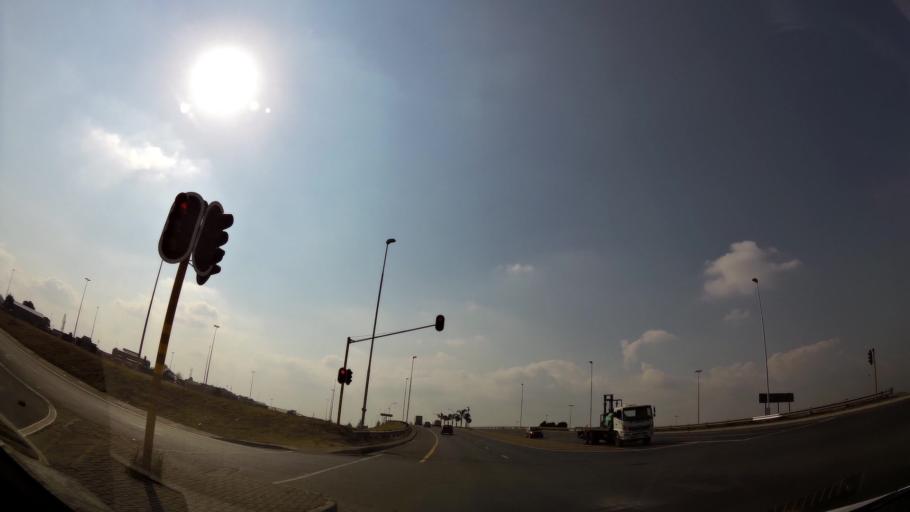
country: ZA
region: Gauteng
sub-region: Ekurhuleni Metropolitan Municipality
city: Germiston
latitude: -26.1767
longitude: 28.1967
